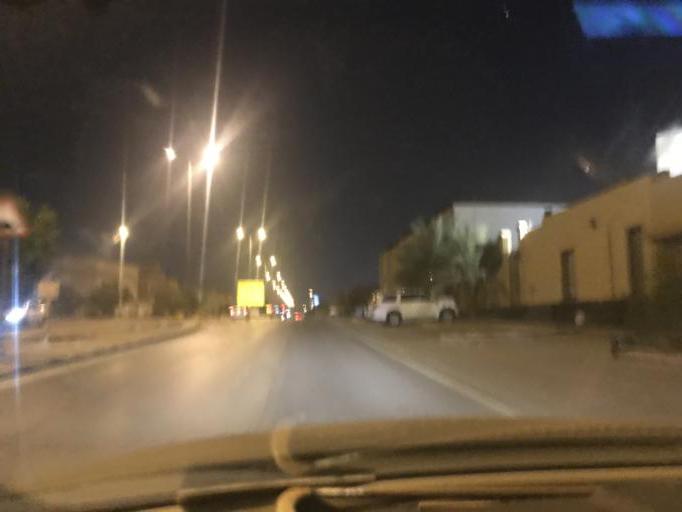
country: SA
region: Ar Riyad
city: Riyadh
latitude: 24.6772
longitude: 46.7860
